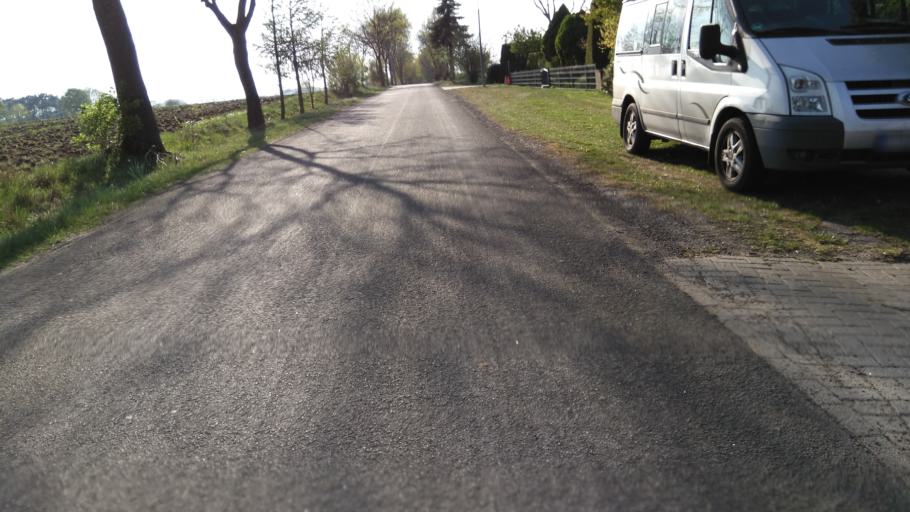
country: DE
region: Lower Saxony
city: Buxtehude
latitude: 53.4365
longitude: 9.6866
